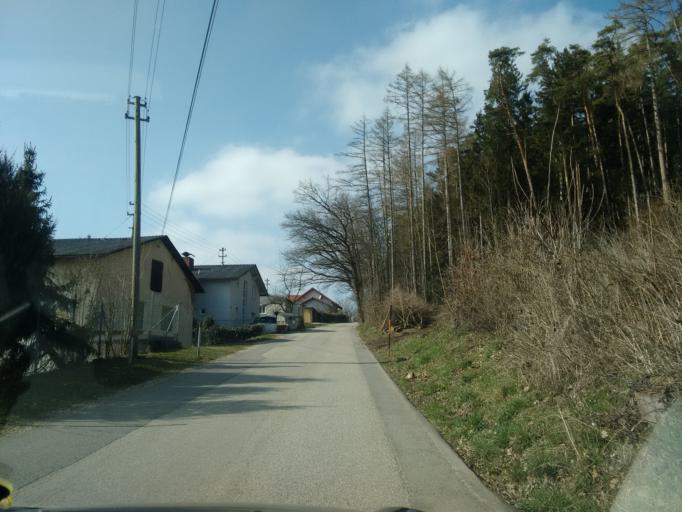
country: AT
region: Upper Austria
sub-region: Politischer Bezirk Grieskirchen
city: Bad Schallerbach
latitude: 48.1957
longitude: 13.9660
